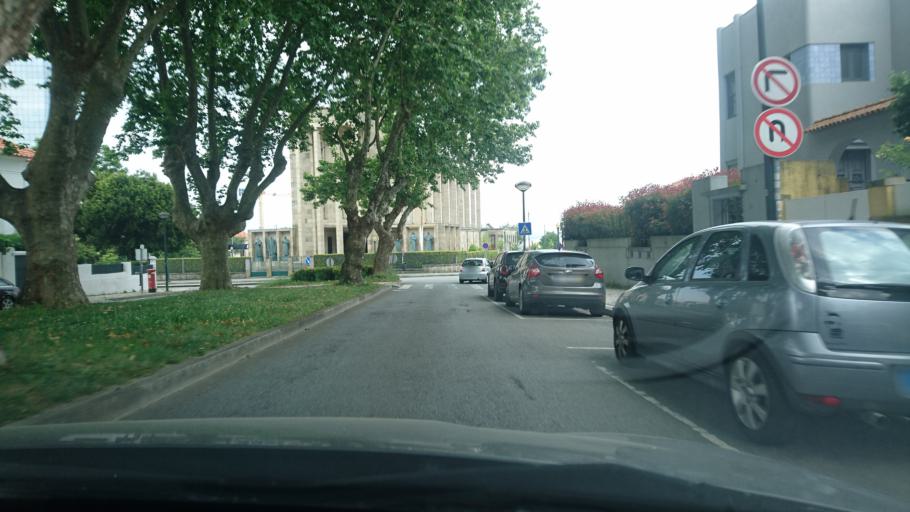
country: PT
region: Porto
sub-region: Porto
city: Porto
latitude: 41.1645
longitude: -8.5911
